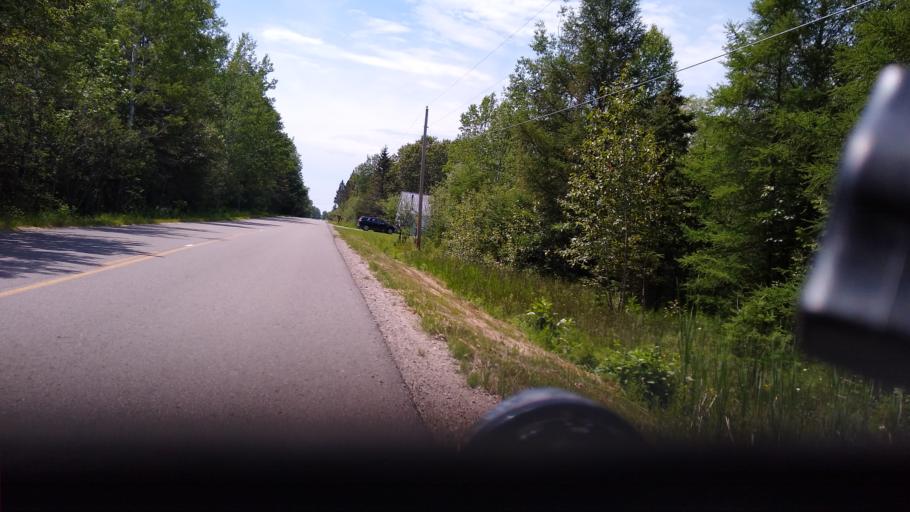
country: US
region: Michigan
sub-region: Delta County
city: Escanaba
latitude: 45.7101
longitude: -87.1244
